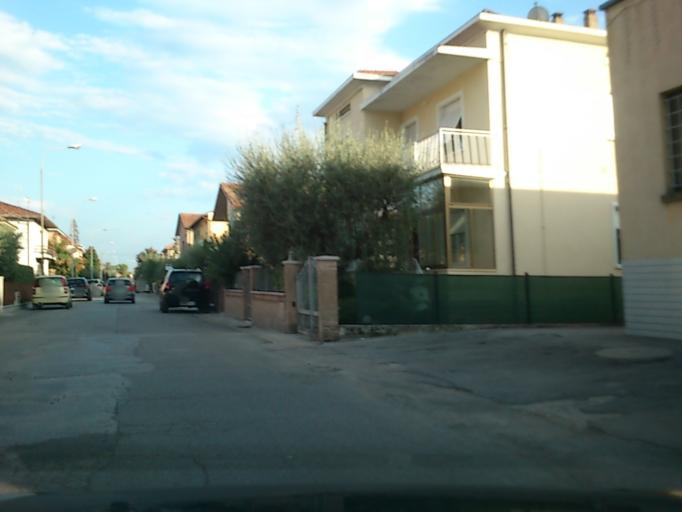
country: IT
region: The Marches
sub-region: Provincia di Pesaro e Urbino
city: Centinarola
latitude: 43.8341
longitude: 12.9972
